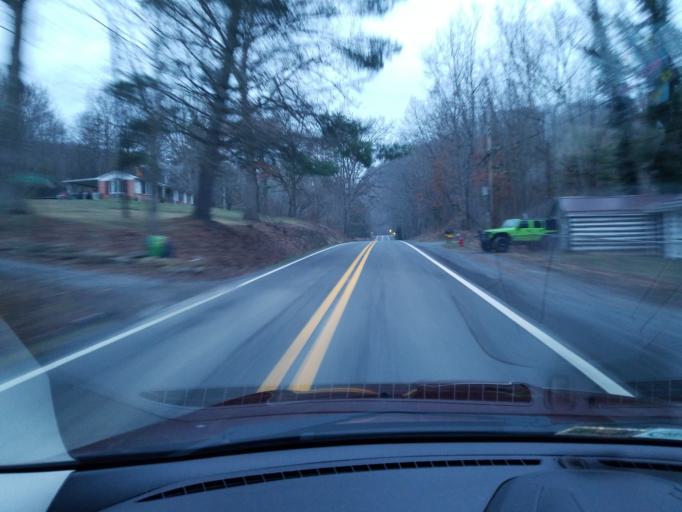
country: US
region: West Virginia
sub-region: Greenbrier County
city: Fairlea
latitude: 37.7556
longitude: -80.4014
